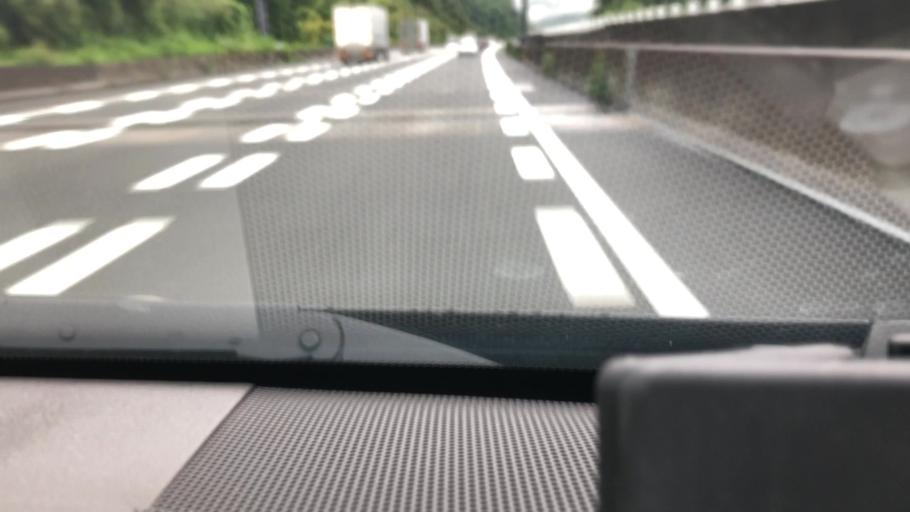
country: JP
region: Shizuoka
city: Shizuoka-shi
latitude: 35.0333
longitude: 138.3627
